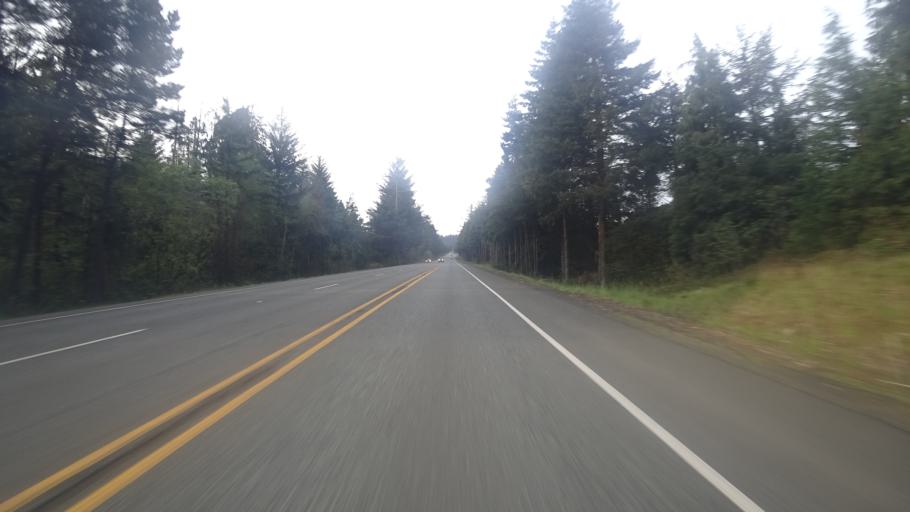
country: US
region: Oregon
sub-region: Coos County
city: Lakeside
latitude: 43.5027
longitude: -124.2183
